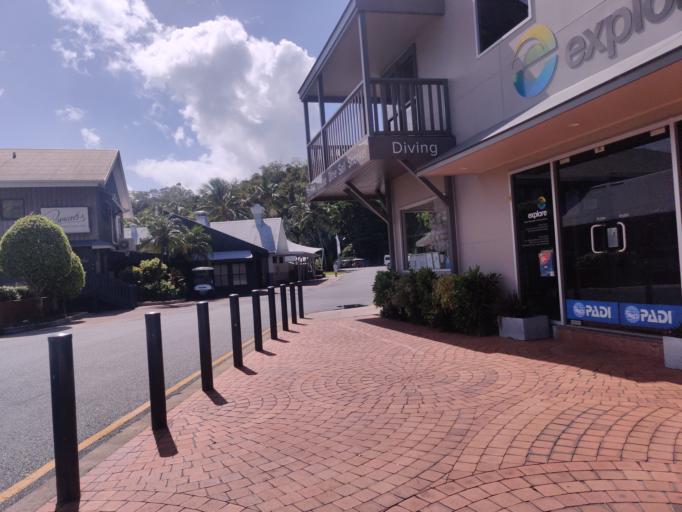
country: AU
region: Queensland
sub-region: Whitsunday
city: Proserpine
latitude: -20.3454
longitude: 148.9512
